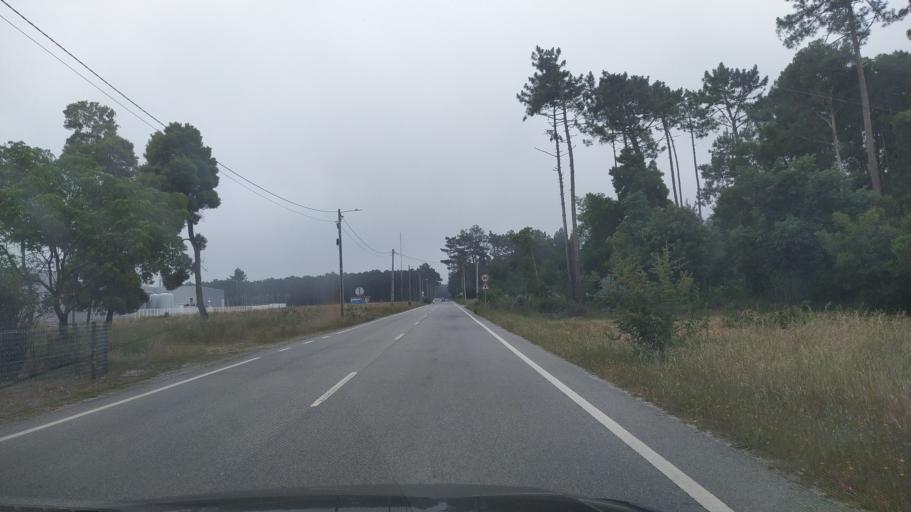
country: PT
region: Aveiro
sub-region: Ilhavo
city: Gafanha da Encarnacao
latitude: 40.6038
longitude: -8.7224
